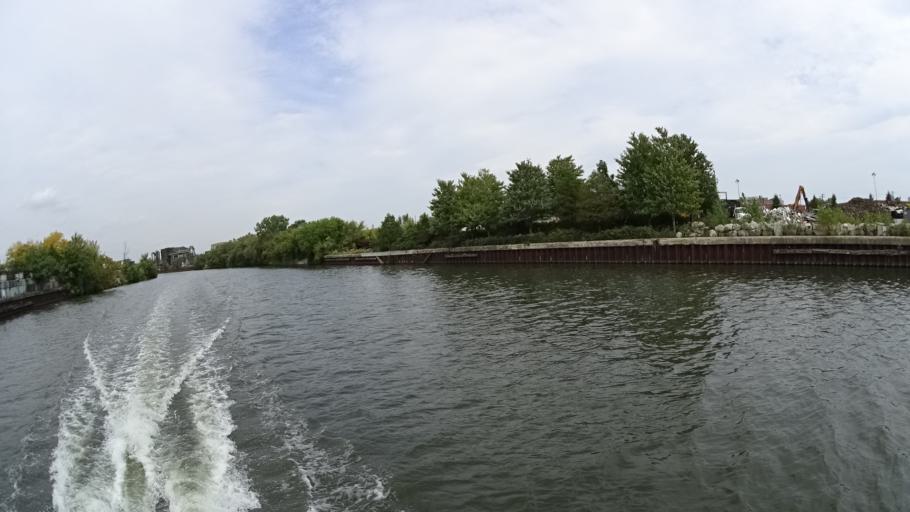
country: US
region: Illinois
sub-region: Cook County
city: Chicago
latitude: 41.9121
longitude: -87.6575
